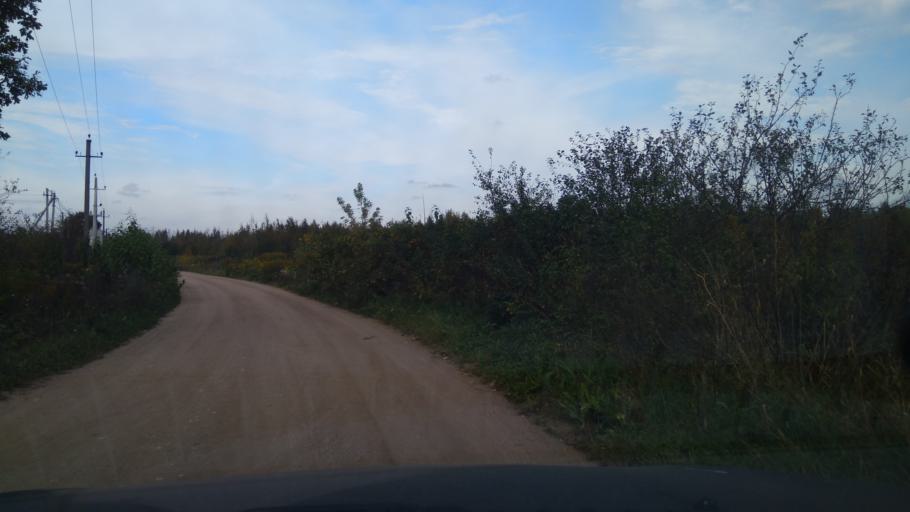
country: BY
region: Minsk
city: Rudzyensk
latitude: 53.6084
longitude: 27.8483
